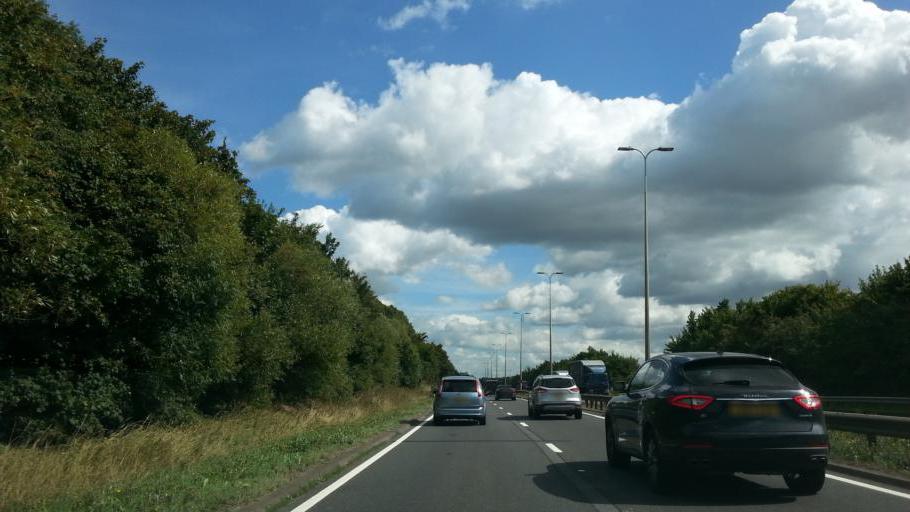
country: GB
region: England
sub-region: Essex
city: Pitsea
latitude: 51.5563
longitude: 0.4871
